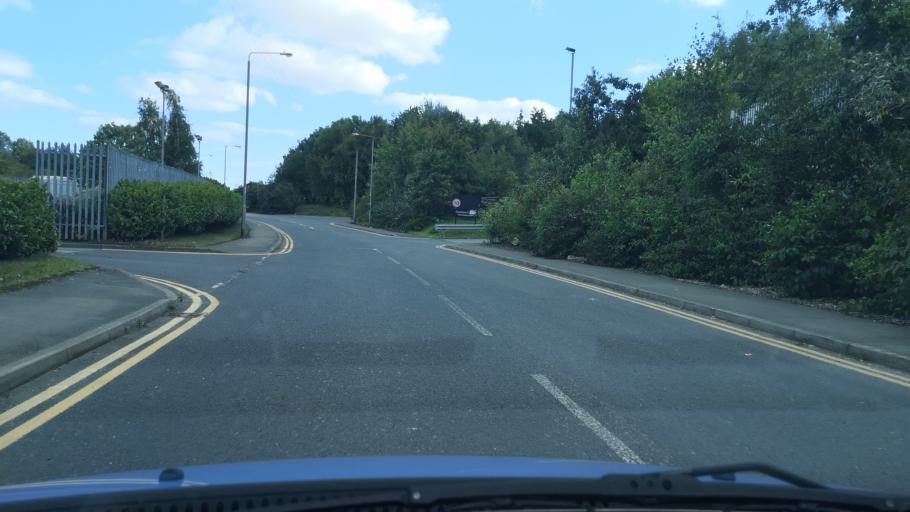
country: GB
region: England
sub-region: City and Borough of Wakefield
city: South Elmsall
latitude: 53.6012
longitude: -1.2685
